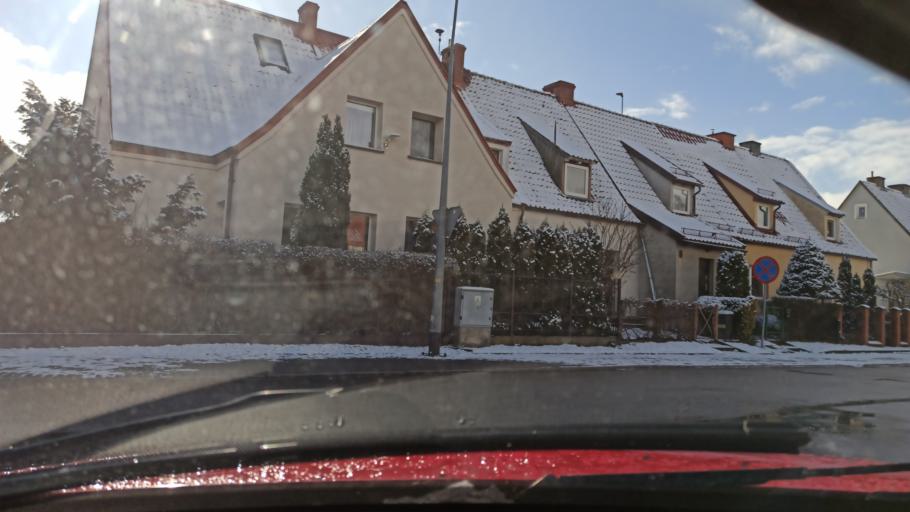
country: PL
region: Warmian-Masurian Voivodeship
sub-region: Powiat elblaski
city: Elblag
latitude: 54.1450
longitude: 19.4073
